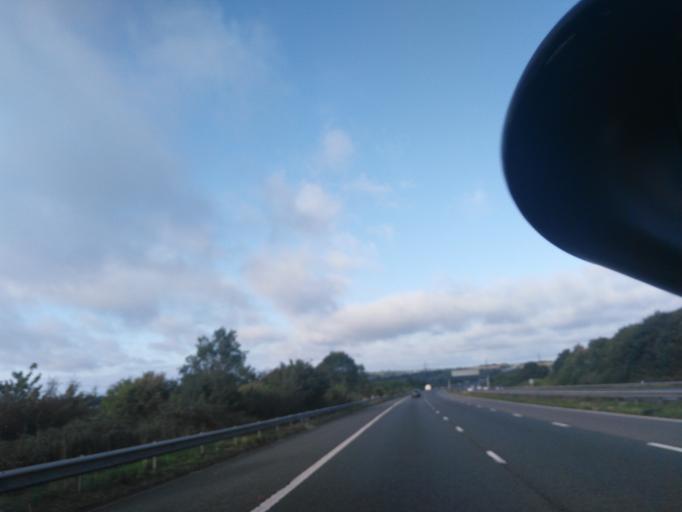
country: GB
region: England
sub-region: South Gloucestershire
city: Hinton
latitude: 51.4988
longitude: -2.3723
